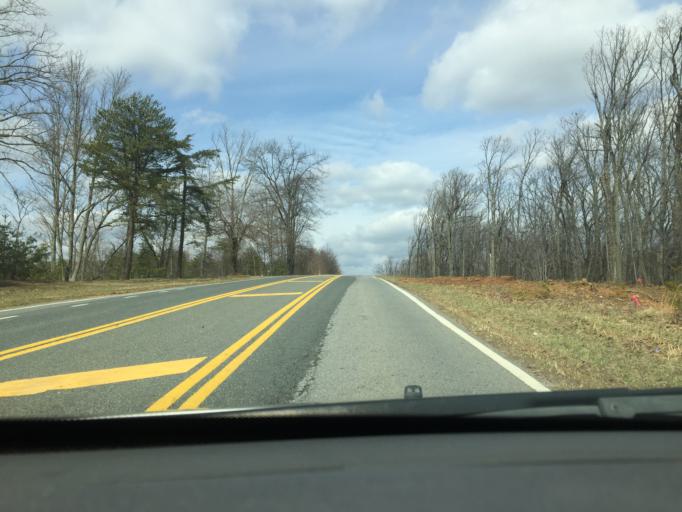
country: US
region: Virginia
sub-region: City of Lynchburg
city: West Lynchburg
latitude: 37.3397
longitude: -79.1744
